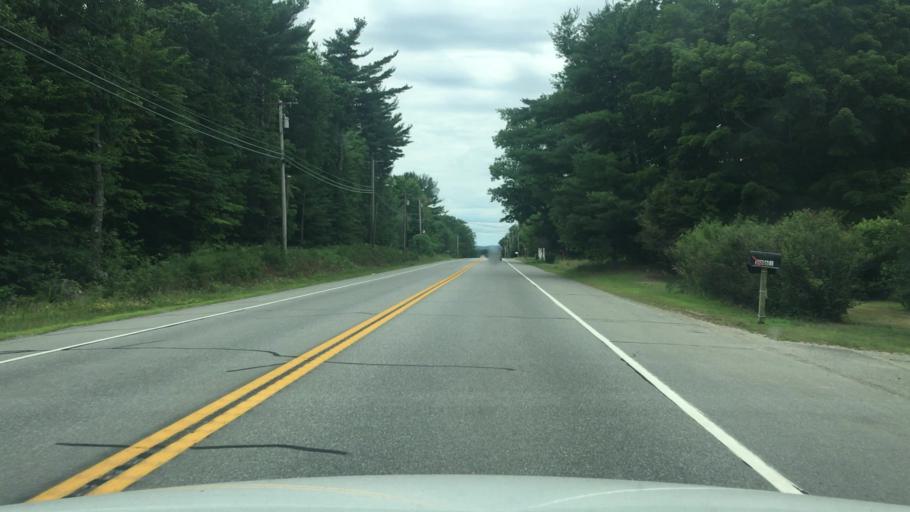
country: US
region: Maine
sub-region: Kennebec County
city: Sidney
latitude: 44.3358
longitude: -69.6834
